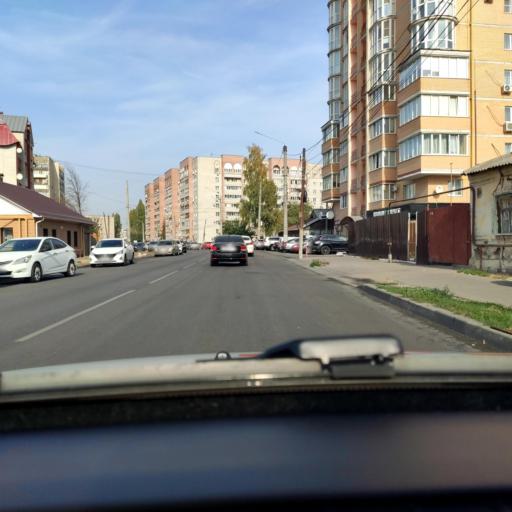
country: RU
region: Voronezj
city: Voronezh
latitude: 51.6507
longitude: 39.1864
